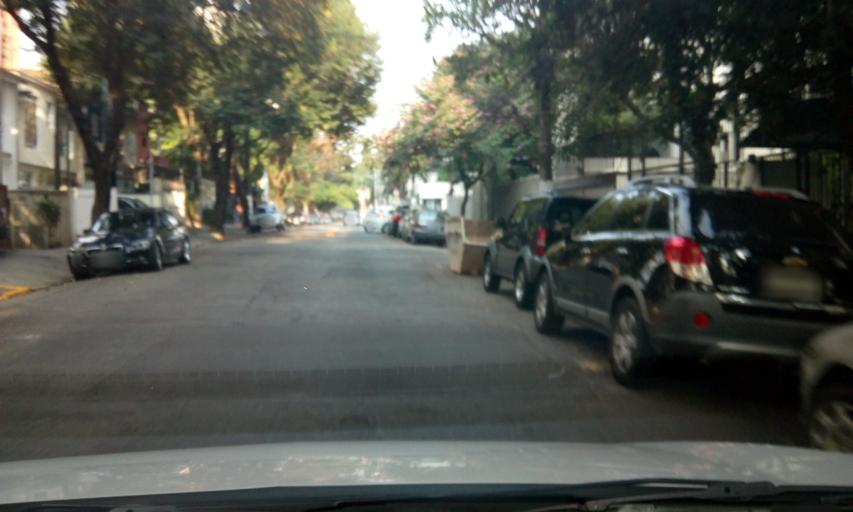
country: BR
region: Sao Paulo
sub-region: Sao Paulo
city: Sao Paulo
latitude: -23.6110
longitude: -46.6610
